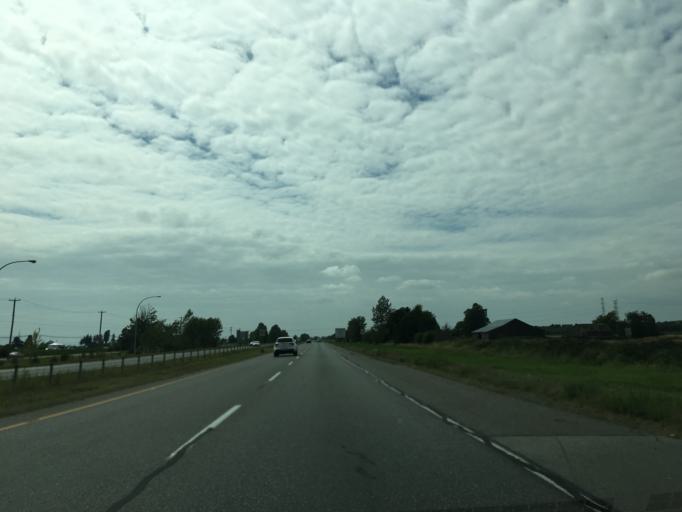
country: CA
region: British Columbia
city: Delta
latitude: 49.0905
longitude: -122.9672
